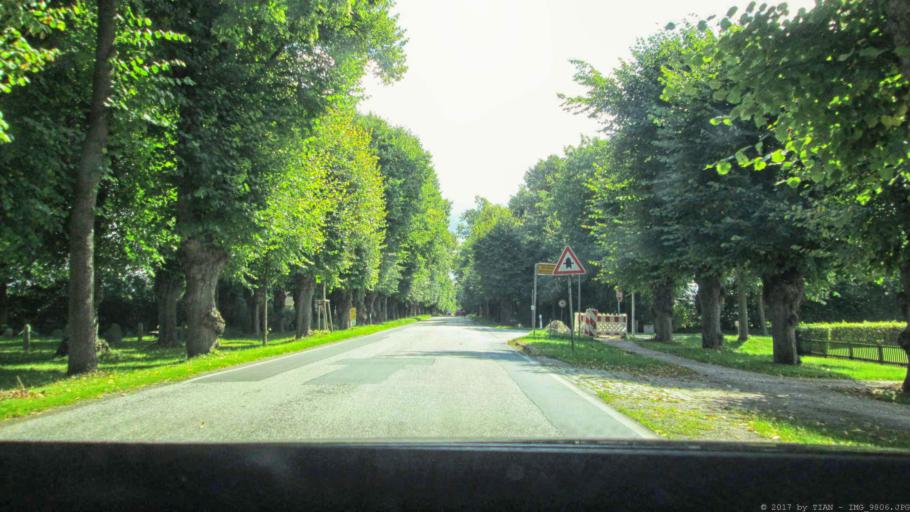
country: DE
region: Schleswig-Holstein
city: Jersbek
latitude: 53.7460
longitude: 10.2135
